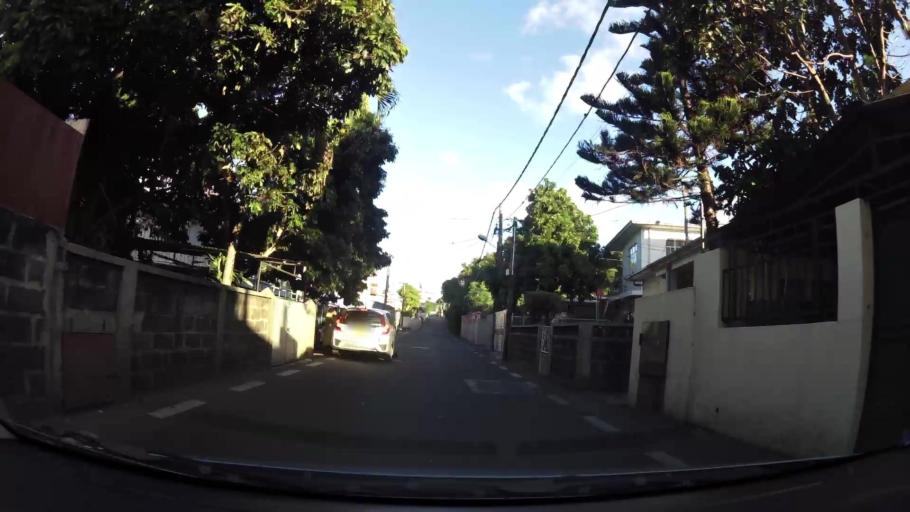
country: MU
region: Plaines Wilhems
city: Quatre Bornes
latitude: -20.2488
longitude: 57.4693
